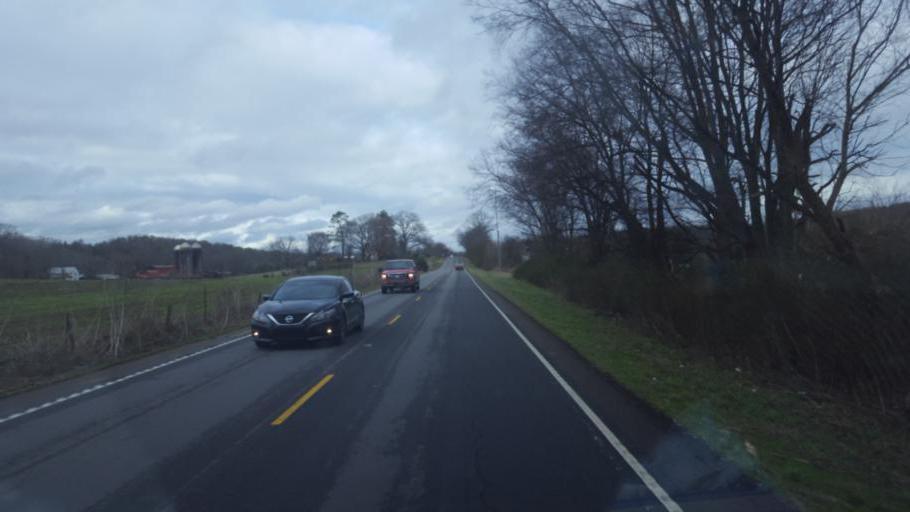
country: US
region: Tennessee
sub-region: McMinn County
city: Athens
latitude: 35.3520
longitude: -84.7126
